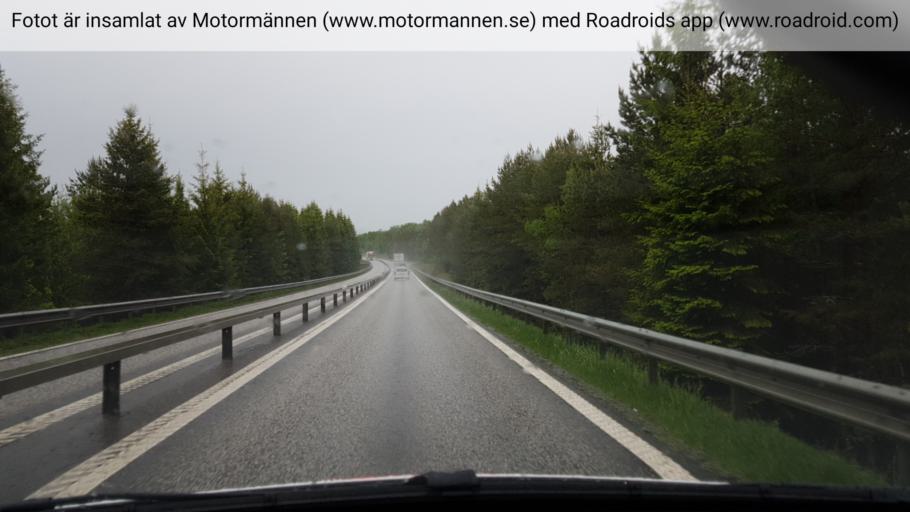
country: SE
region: Joenkoeping
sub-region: Jonkopings Kommun
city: Jonkoping
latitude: 57.7853
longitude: 14.1024
